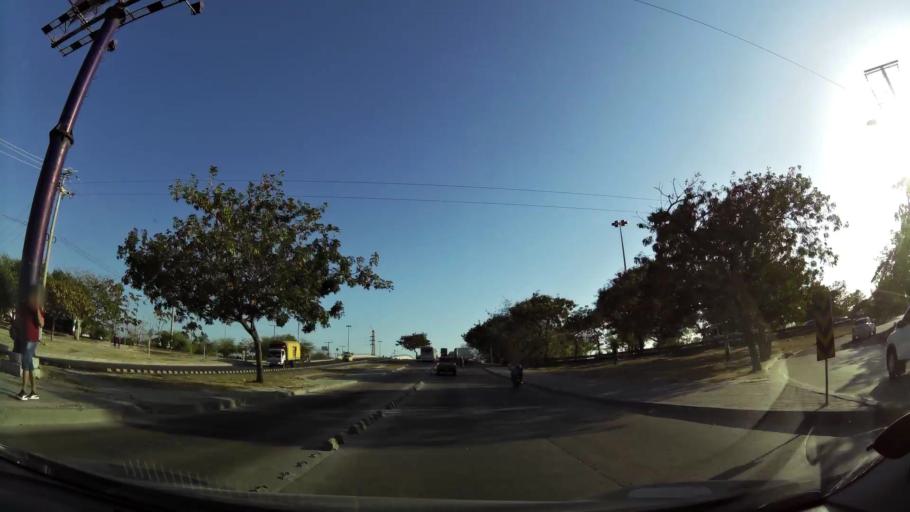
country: CO
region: Atlantico
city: Soledad
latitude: 10.9252
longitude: -74.7992
